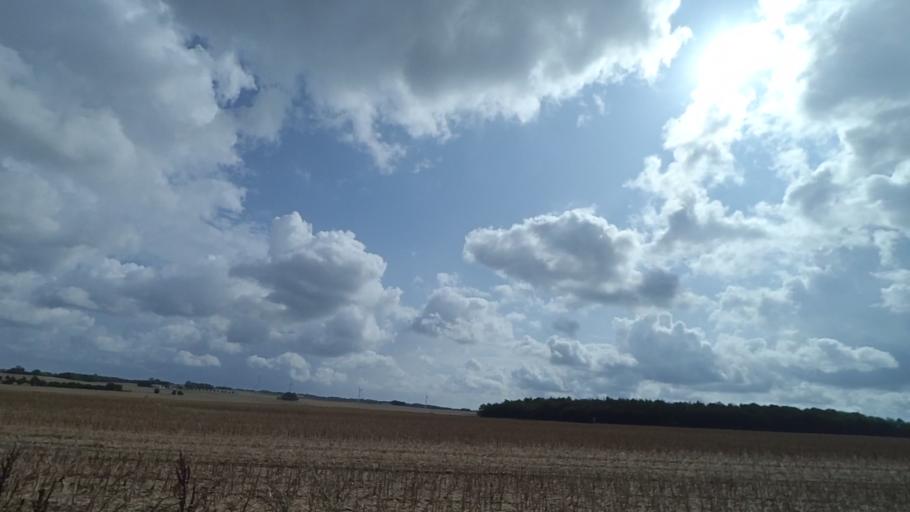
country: DK
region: Central Jutland
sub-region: Norddjurs Kommune
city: Auning
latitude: 56.4897
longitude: 10.4432
